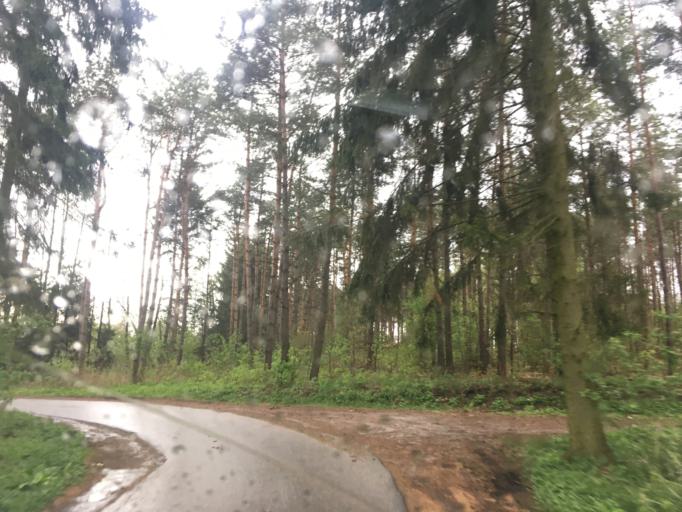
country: PL
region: Warmian-Masurian Voivodeship
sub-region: Powiat dzialdowski
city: Rybno
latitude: 53.3837
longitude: 19.9866
